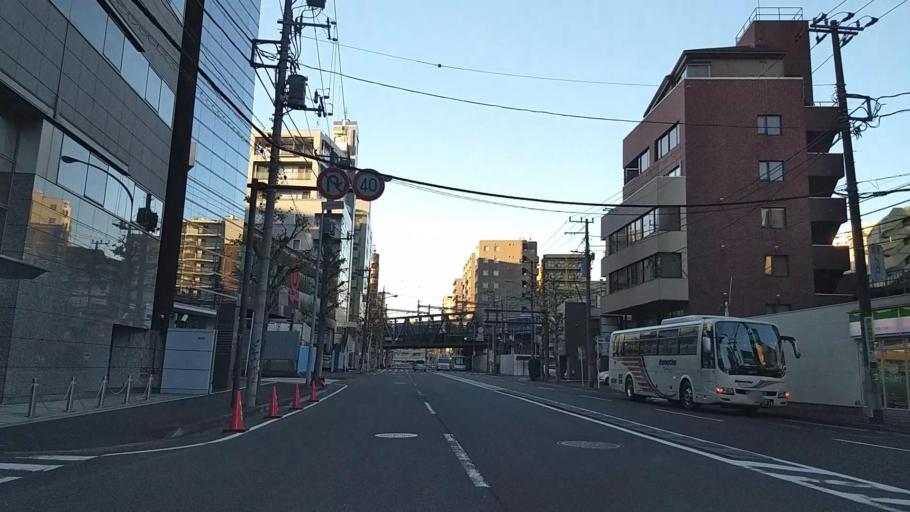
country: JP
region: Kanagawa
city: Yokohama
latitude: 35.4598
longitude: 139.6195
